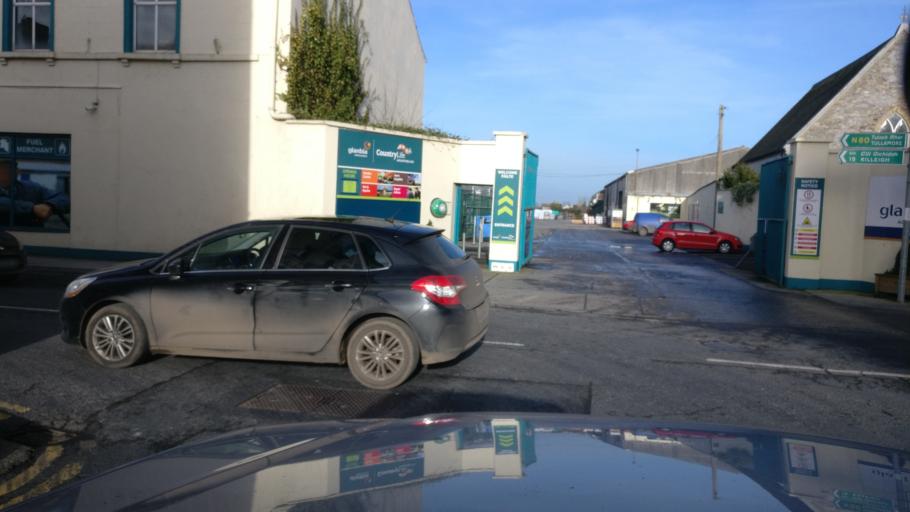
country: IE
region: Leinster
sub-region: Laois
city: Mountmellick
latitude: 53.1168
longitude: -7.3258
